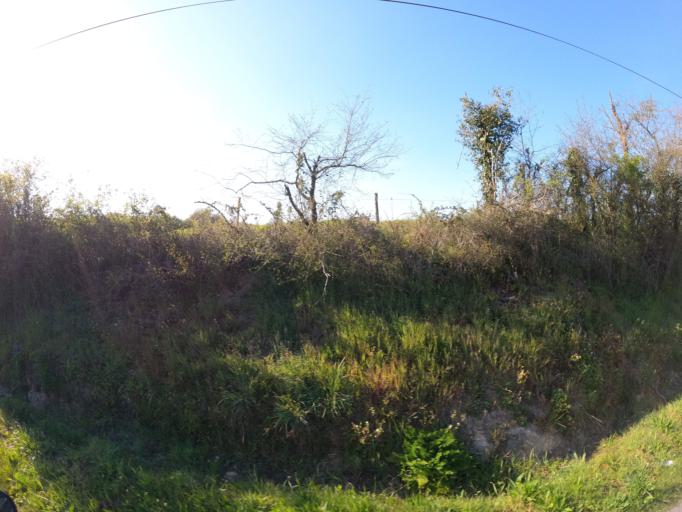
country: FR
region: Pays de la Loire
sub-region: Departement de la Vendee
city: Beaurepaire
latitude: 46.9133
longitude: -1.1264
